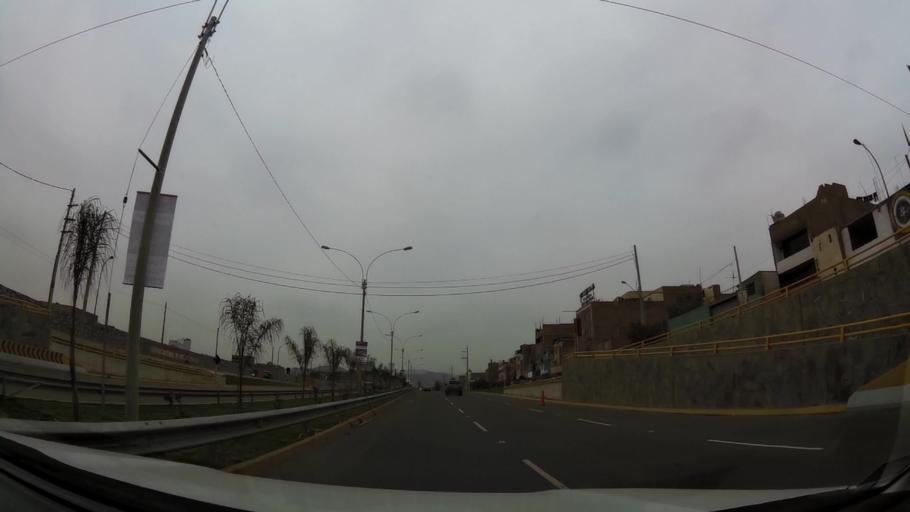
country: PE
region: Lima
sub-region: Lima
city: Vitarte
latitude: -12.0440
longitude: -76.9327
